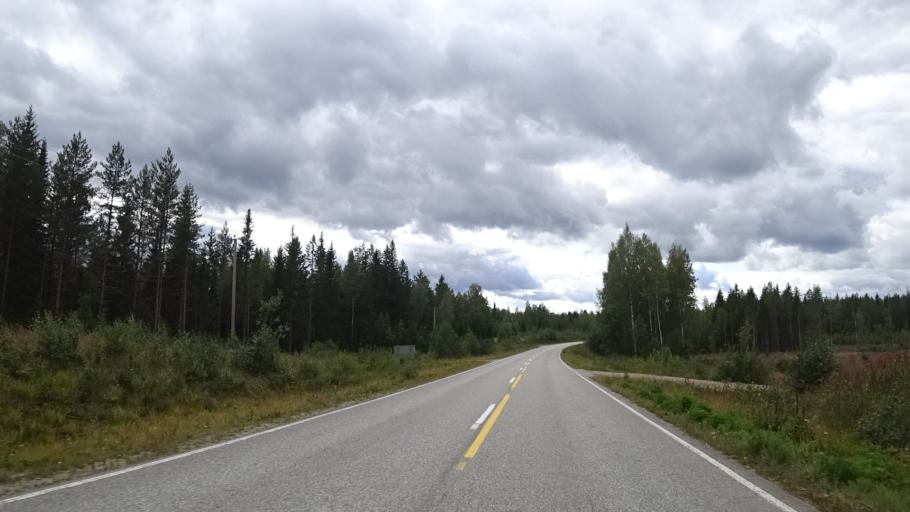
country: FI
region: North Karelia
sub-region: Joensuu
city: Ilomantsi
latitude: 62.6302
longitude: 31.2733
